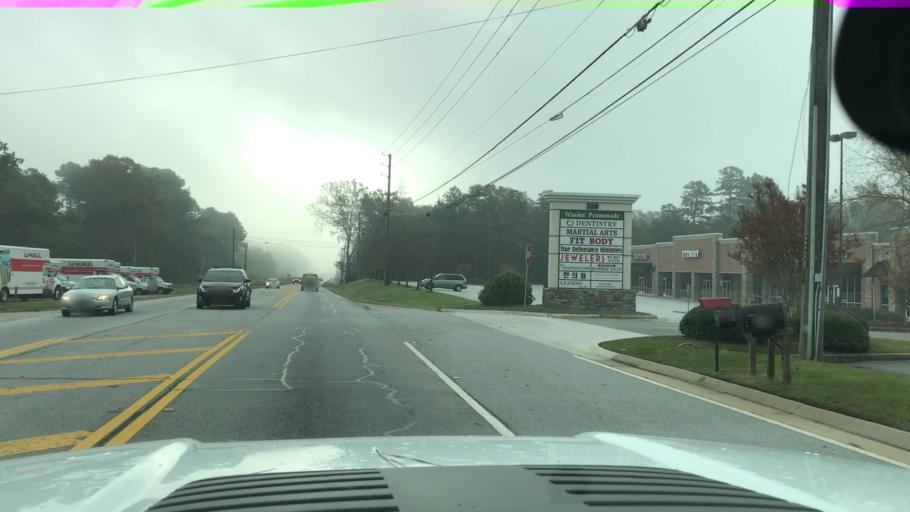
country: US
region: Georgia
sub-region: Barrow County
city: Russell
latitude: 33.9786
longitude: -83.7067
